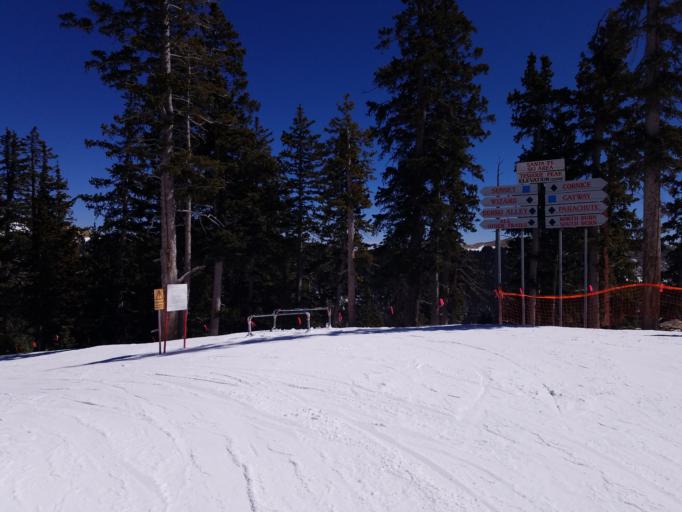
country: US
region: New Mexico
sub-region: Santa Fe County
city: Santa Fe
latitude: 35.7874
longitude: -105.7817
